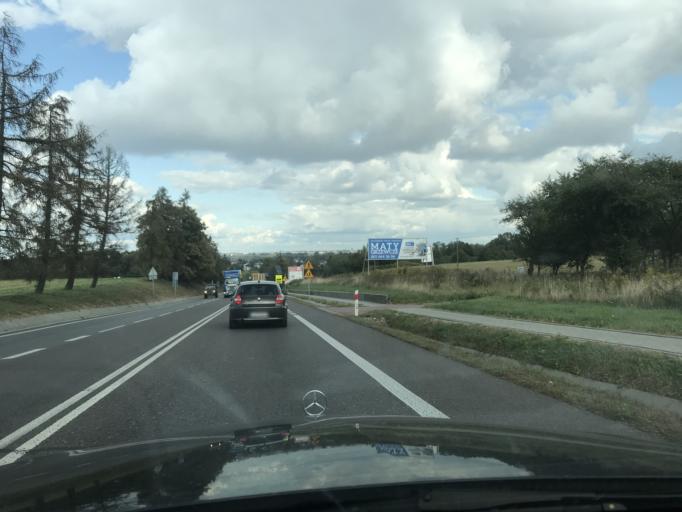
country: PL
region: Lublin Voivodeship
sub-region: Powiat lubelski
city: Jakubowice Murowane
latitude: 51.3136
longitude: 22.6022
